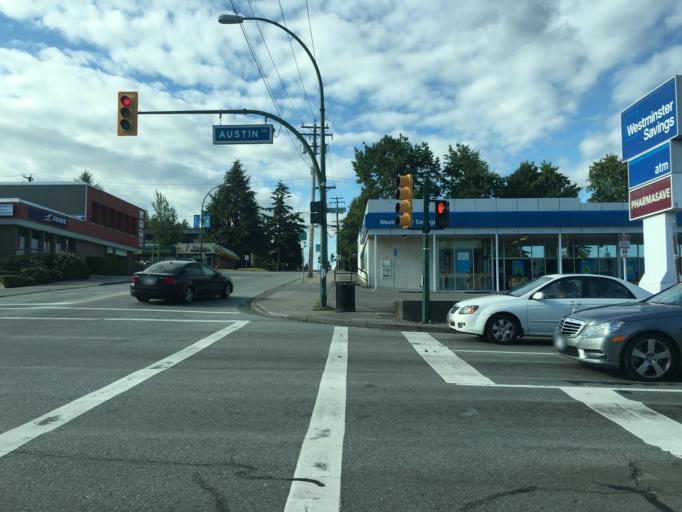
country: CA
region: British Columbia
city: Port Moody
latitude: 49.2489
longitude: -122.8621
